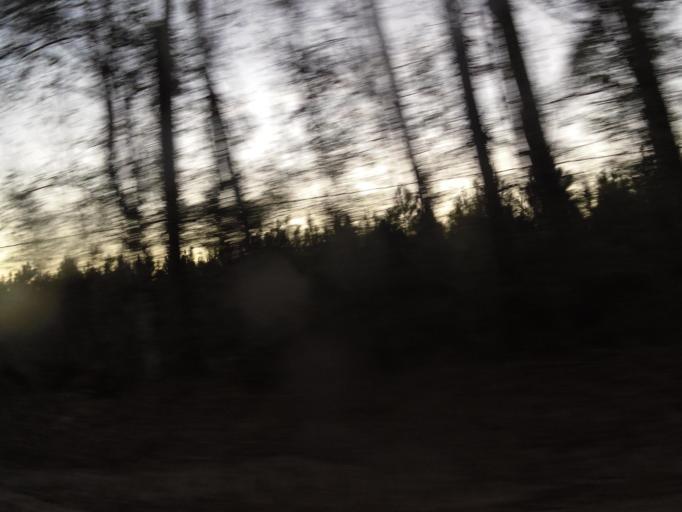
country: US
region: Florida
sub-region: Clay County
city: Asbury Lake
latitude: 29.9779
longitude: -81.7941
